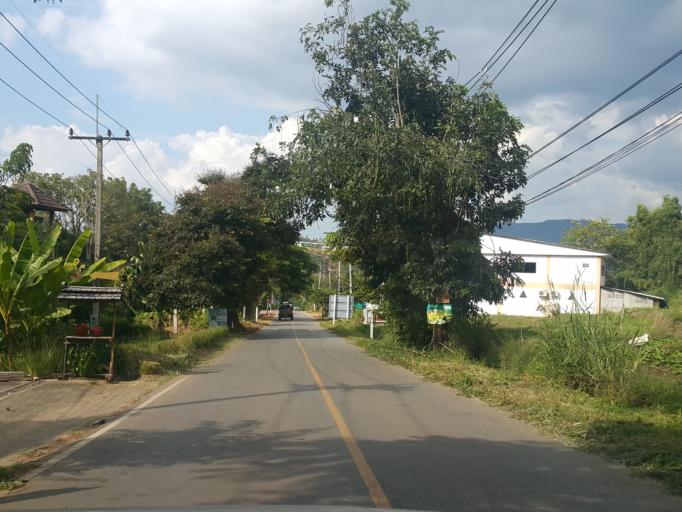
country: TH
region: Chiang Mai
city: Mae Chaem
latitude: 18.4869
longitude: 98.3775
